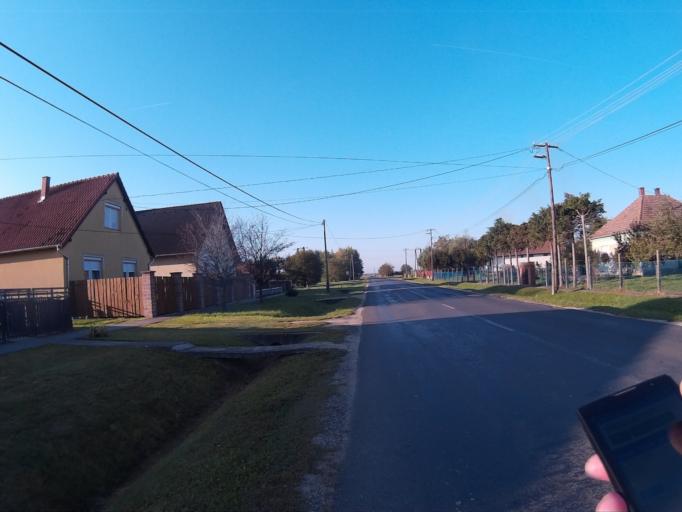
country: HU
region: Vas
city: Jak
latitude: 47.1323
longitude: 16.5827
